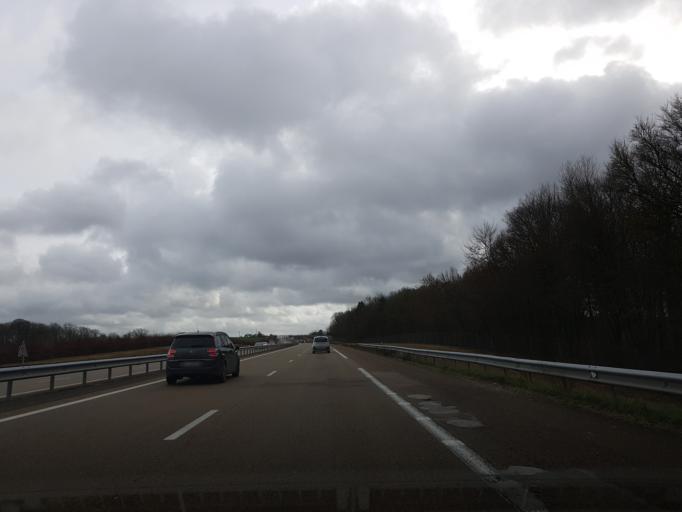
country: FR
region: Champagne-Ardenne
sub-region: Departement de la Haute-Marne
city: Chamarandes-Choignes
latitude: 47.9852
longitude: 5.1290
